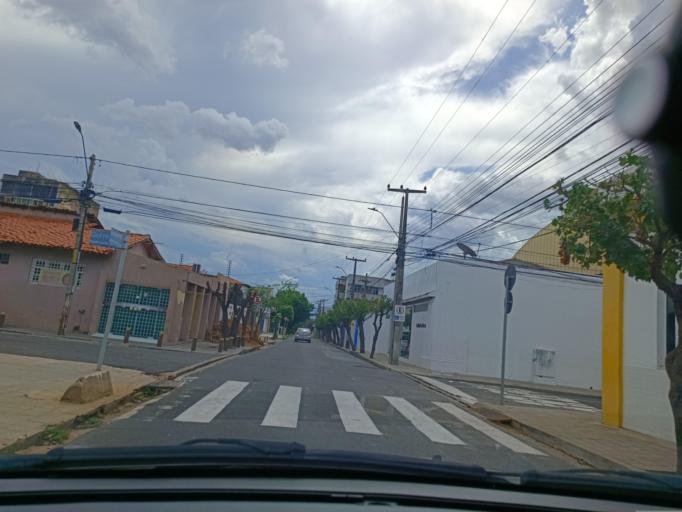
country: BR
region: Piaui
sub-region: Teresina
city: Teresina
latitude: -5.0848
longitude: -42.8134
